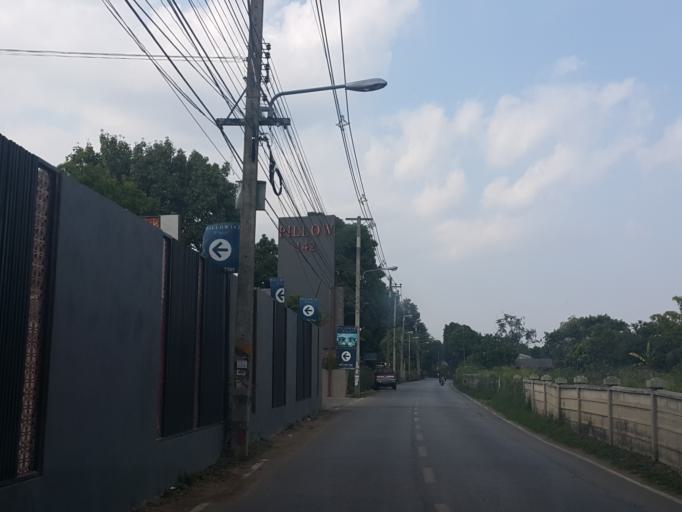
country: TH
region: Chiang Mai
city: Chiang Mai
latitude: 18.8187
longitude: 98.9973
